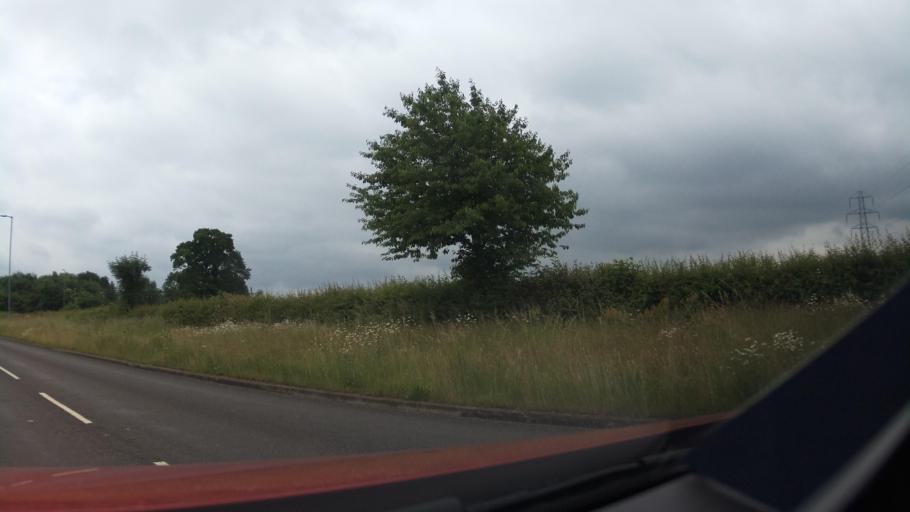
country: GB
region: England
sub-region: District of Rutland
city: Oakham
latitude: 52.6604
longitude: -0.7189
